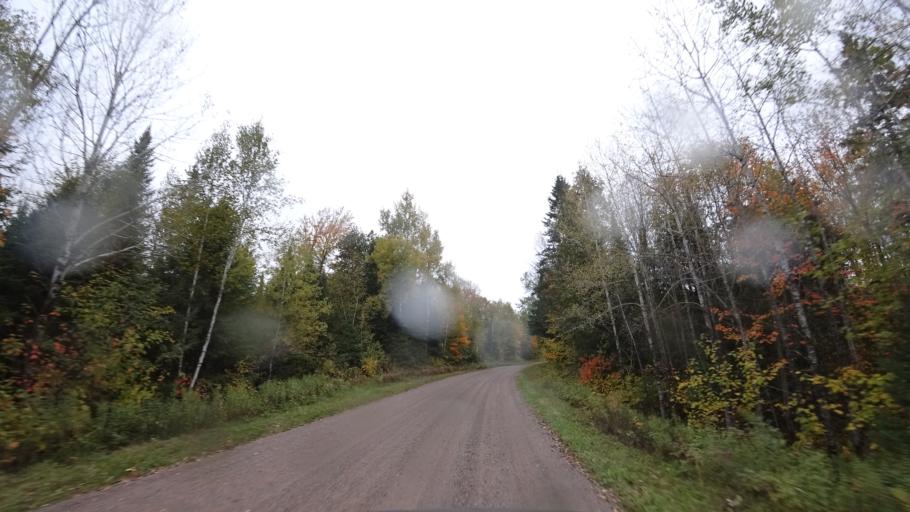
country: US
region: Wisconsin
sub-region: Sawyer County
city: Little Round Lake
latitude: 45.9833
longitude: -90.9993
